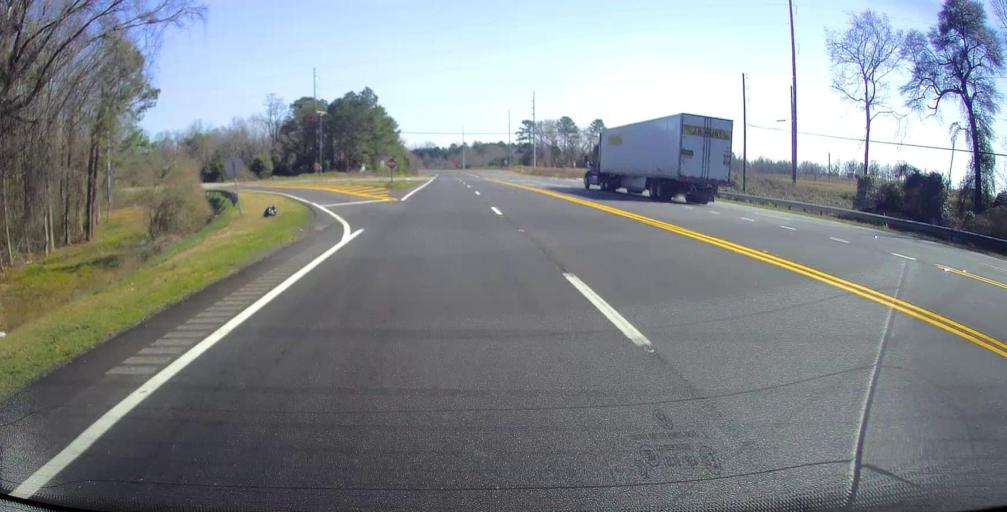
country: US
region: Georgia
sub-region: Houston County
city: Perry
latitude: 32.4908
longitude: -83.7375
